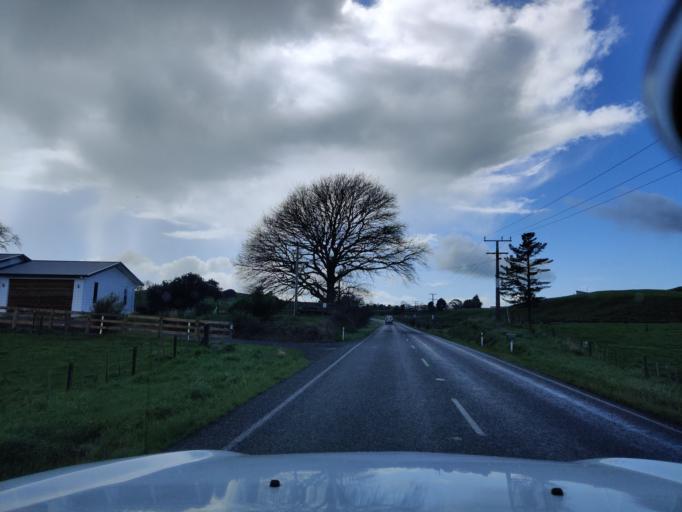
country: NZ
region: Waikato
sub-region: Waikato District
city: Ngaruawahia
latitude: -37.5791
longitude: 175.2243
